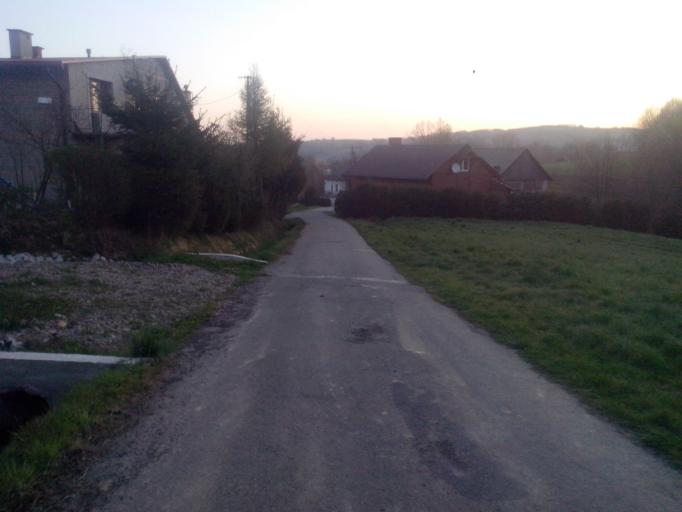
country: PL
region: Subcarpathian Voivodeship
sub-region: Powiat strzyzowski
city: Strzyzow
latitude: 49.8362
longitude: 21.8030
